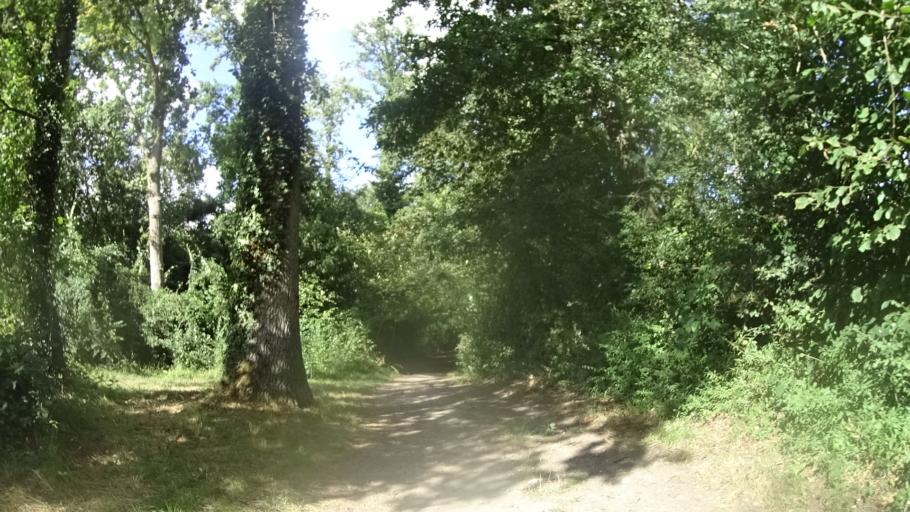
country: FR
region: Ile-de-France
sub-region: Departement de l'Essonne
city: Vert-le-Petit
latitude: 48.5543
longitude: 2.3759
